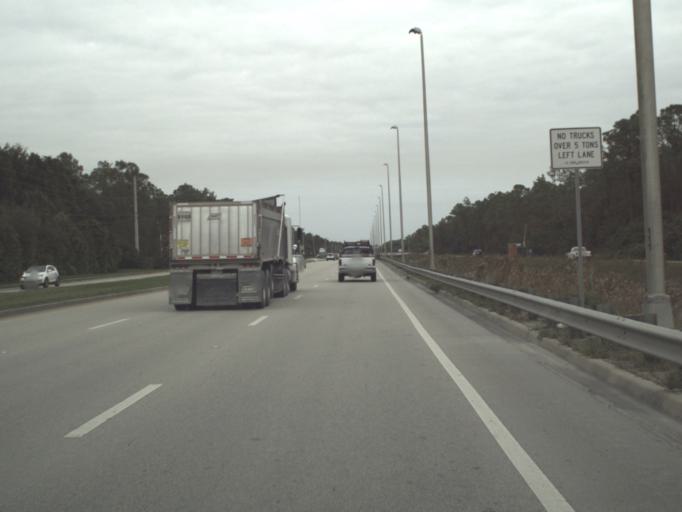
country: US
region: Florida
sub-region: Collier County
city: Lely Resort
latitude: 26.1206
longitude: -81.6869
